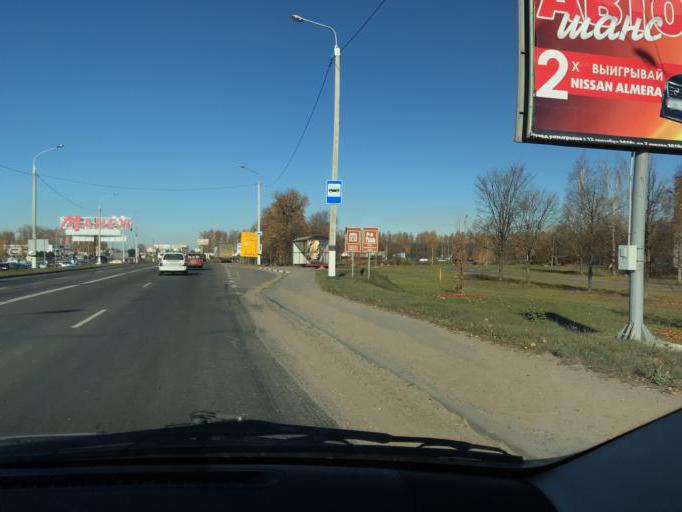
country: BY
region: Vitebsk
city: Polatsk
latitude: 55.4716
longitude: 28.7522
